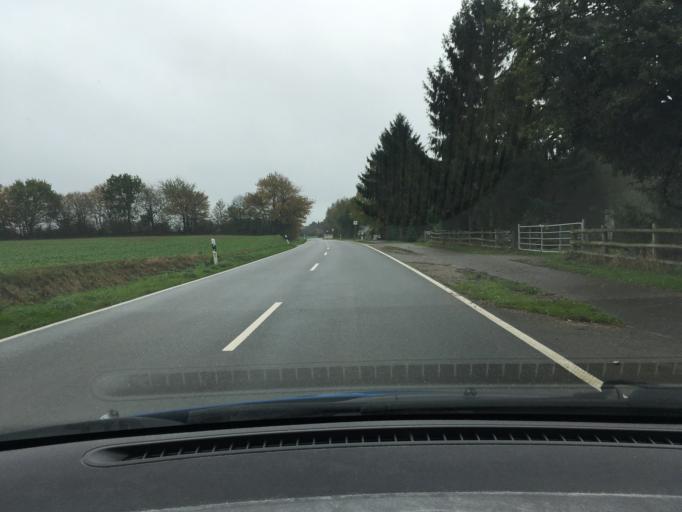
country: DE
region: Schleswig-Holstein
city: Bosdorf
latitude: 54.1164
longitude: 10.4763
